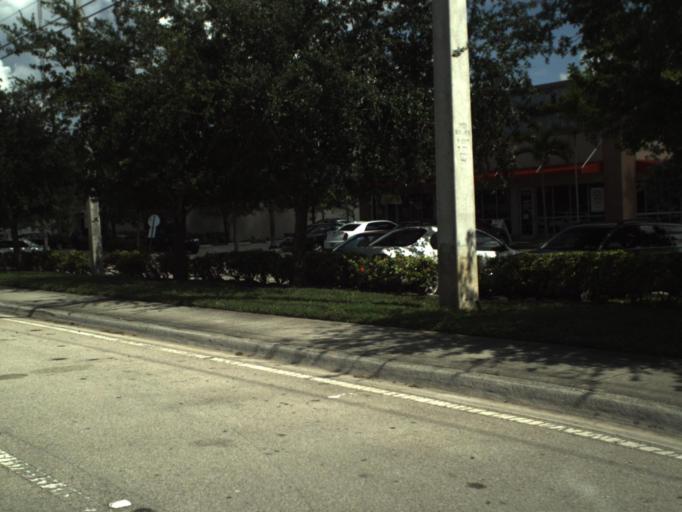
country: US
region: Florida
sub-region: Broward County
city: Pembroke Park
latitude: 25.9955
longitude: -80.1818
